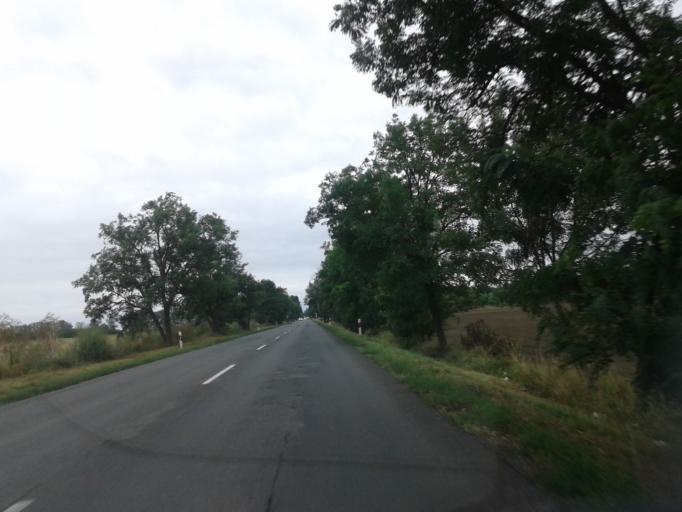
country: HU
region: Pest
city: Dunavarsany
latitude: 47.2550
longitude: 19.0254
